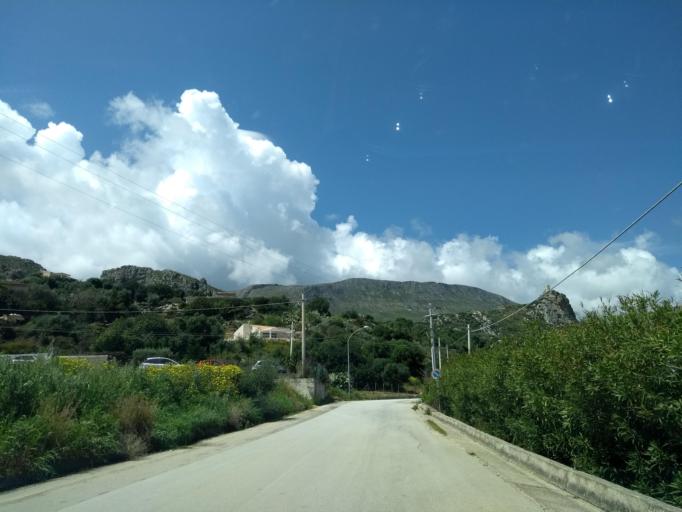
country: IT
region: Sicily
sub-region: Trapani
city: Castellammare del Golfo
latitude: 38.0656
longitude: 12.8200
